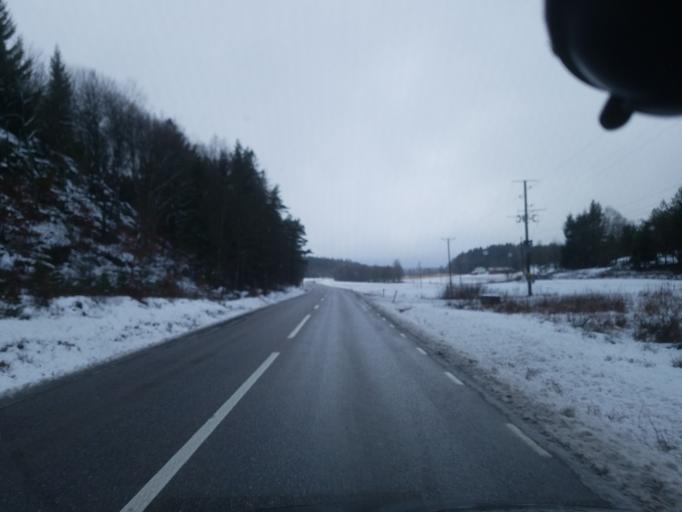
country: SE
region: Vaestra Goetaland
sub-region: Orust
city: Henan
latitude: 58.3129
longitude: 11.6202
